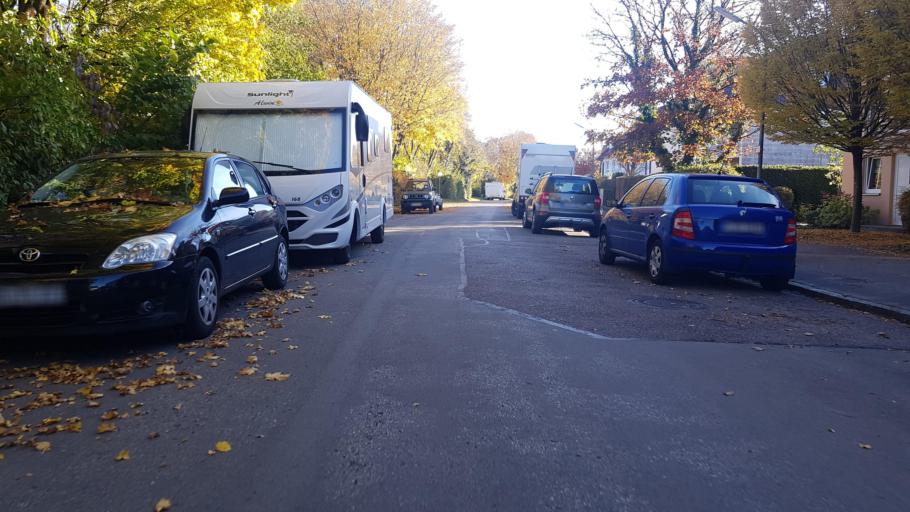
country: DE
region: Bavaria
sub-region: Upper Bavaria
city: Karlsfeld
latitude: 48.1866
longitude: 11.5003
